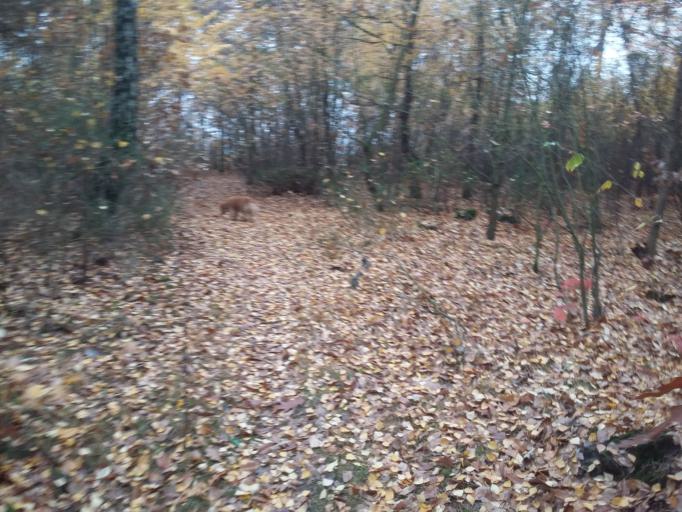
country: PL
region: Lodz Voivodeship
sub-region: Powiat pabianicki
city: Ksawerow
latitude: 51.7211
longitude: 19.3795
